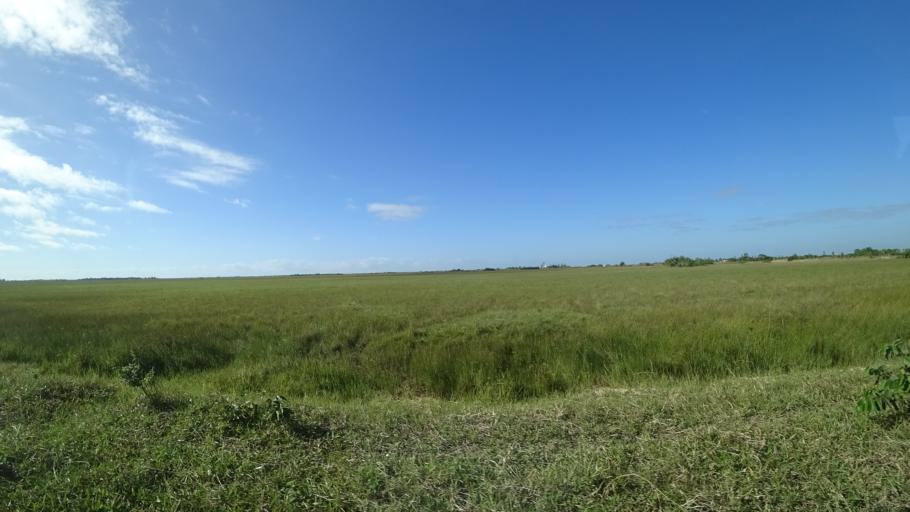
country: MZ
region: Sofala
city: Beira
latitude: -19.7306
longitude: 34.9809
